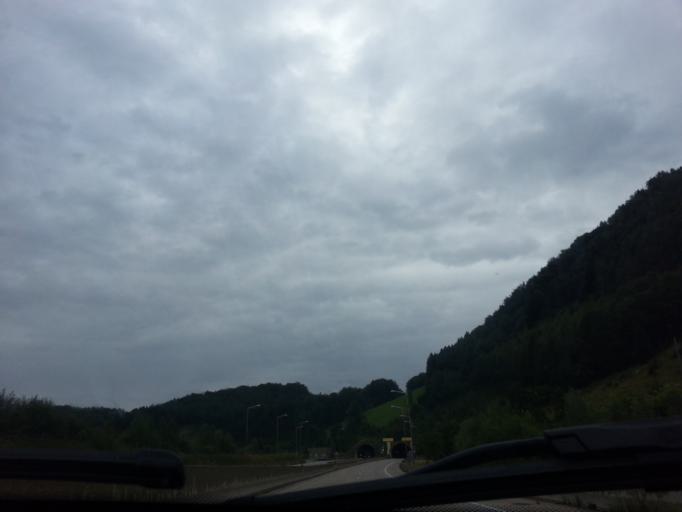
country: AT
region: Upper Austria
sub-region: Politischer Bezirk Kirchdorf an der Krems
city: Micheldorf in Oberoesterreich
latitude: 47.8710
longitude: 14.1220
